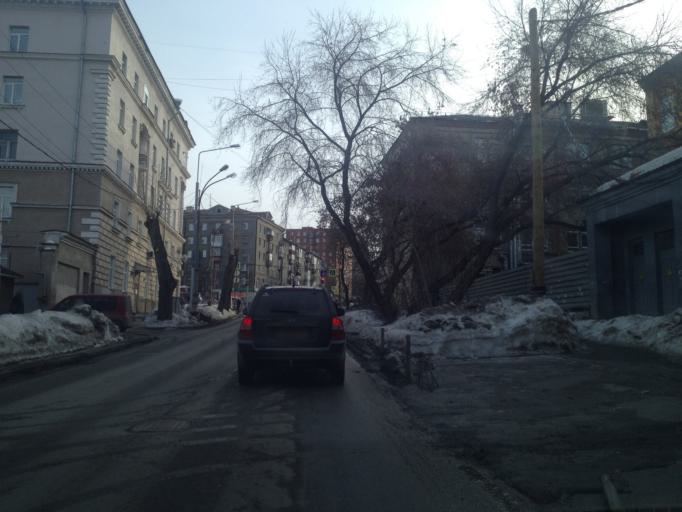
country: RU
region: Sverdlovsk
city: Yekaterinburg
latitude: 56.8408
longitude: 60.5704
